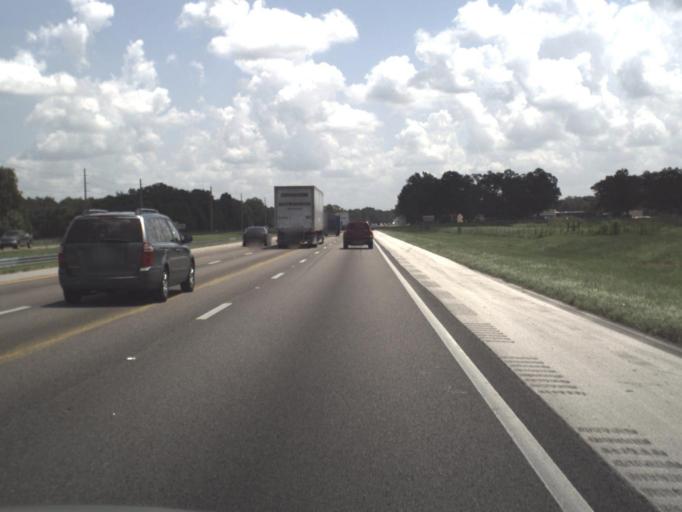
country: US
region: Florida
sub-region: Hillsborough County
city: Dover
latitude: 28.0259
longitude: -82.2291
